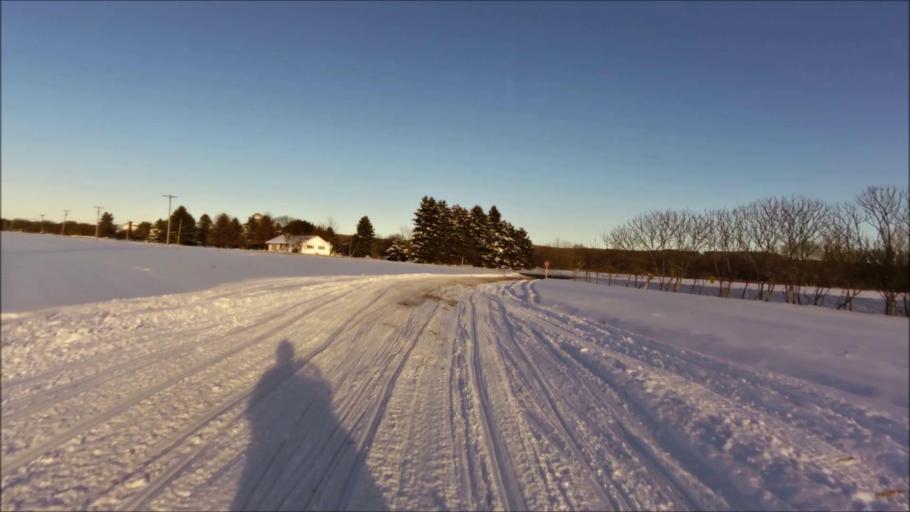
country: US
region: New York
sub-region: Chautauqua County
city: Celoron
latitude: 42.2438
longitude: -79.2840
